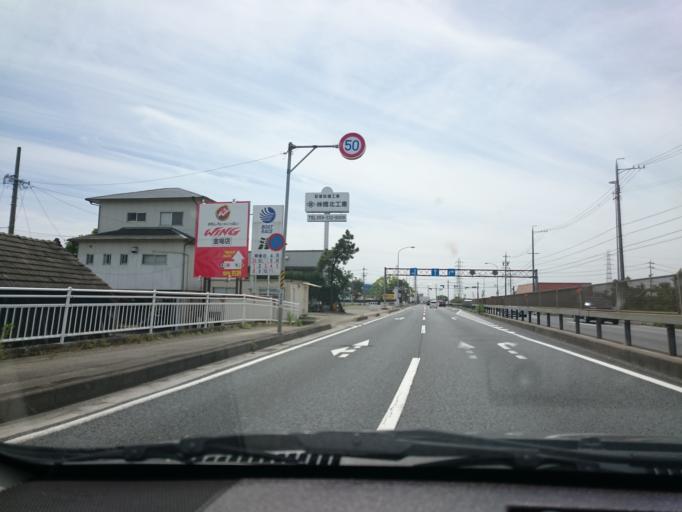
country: JP
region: Mie
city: Yokkaichi
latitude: 34.9892
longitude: 136.6465
